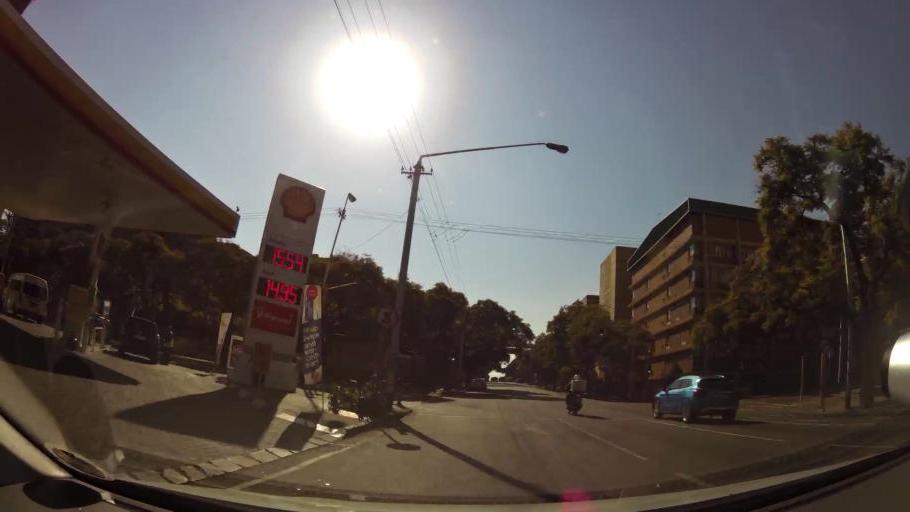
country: ZA
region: Gauteng
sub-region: City of Tshwane Metropolitan Municipality
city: Pretoria
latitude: -25.7426
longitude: 28.2036
